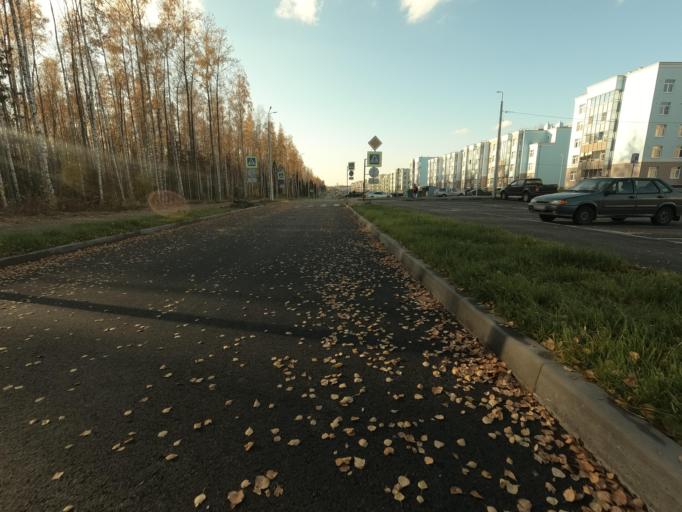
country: RU
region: Leningrad
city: Sertolovo
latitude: 60.1615
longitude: 30.1984
